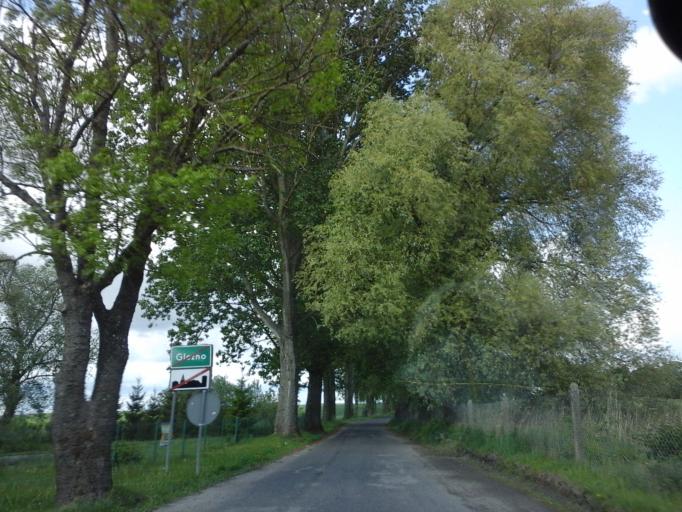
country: PL
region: West Pomeranian Voivodeship
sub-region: Powiat choszczenski
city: Choszczno
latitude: 53.1476
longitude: 15.3525
